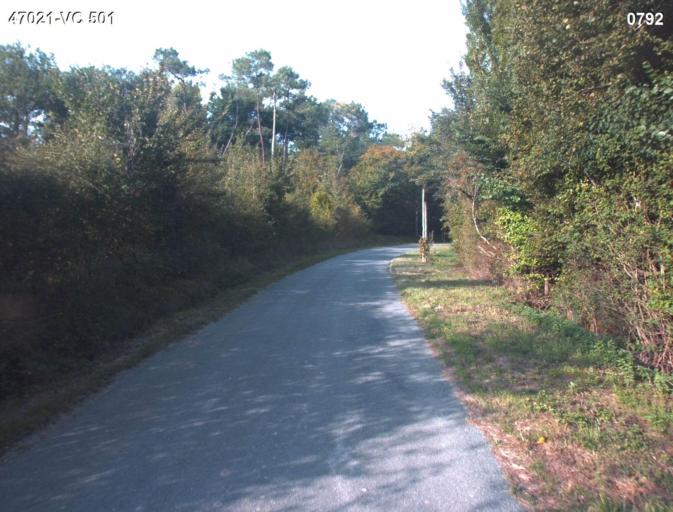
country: FR
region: Aquitaine
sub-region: Departement du Lot-et-Garonne
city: Barbaste
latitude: 44.1847
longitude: 0.2545
